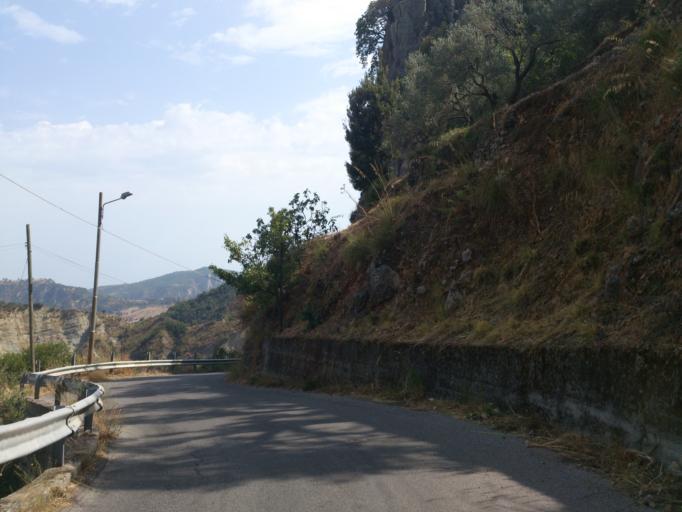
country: IT
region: Calabria
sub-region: Provincia di Reggio Calabria
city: Pazzano
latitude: 38.4698
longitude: 16.4556
